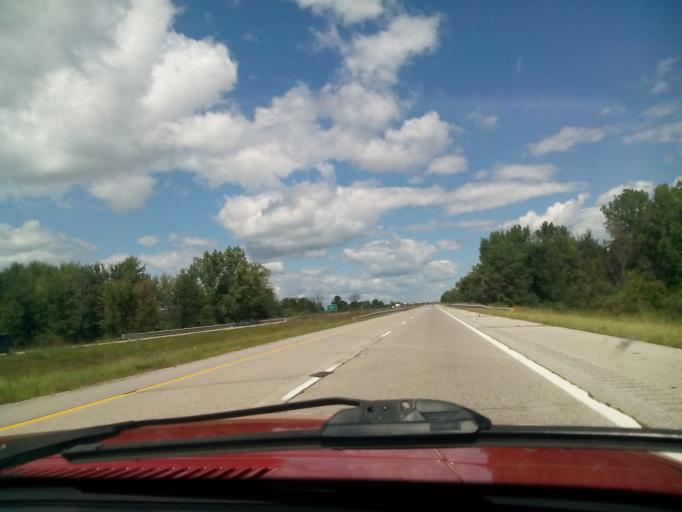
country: US
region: Michigan
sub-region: Bay County
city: Auburn
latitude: 43.6965
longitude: -84.0124
